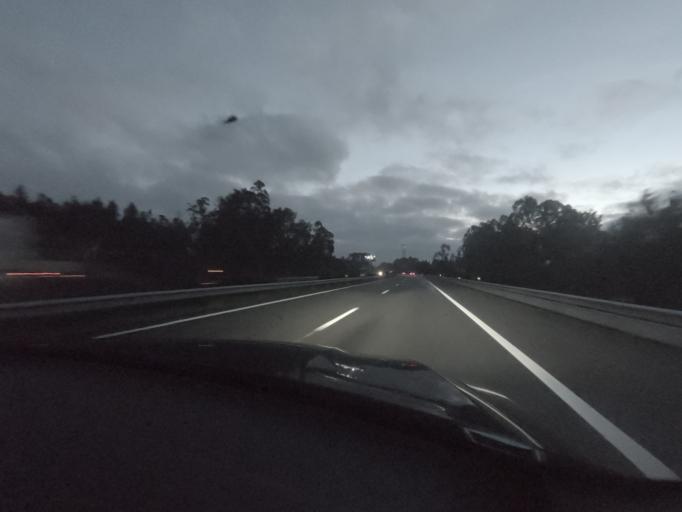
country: PT
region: Leiria
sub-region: Pombal
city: Pombal
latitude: 39.8806
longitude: -8.6977
